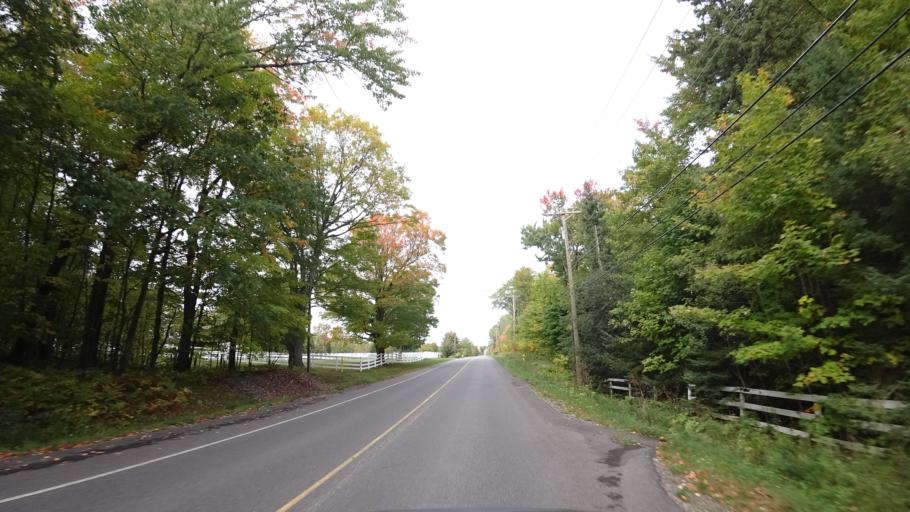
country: US
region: Michigan
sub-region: Marquette County
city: Trowbridge Park
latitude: 46.5384
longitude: -87.4374
